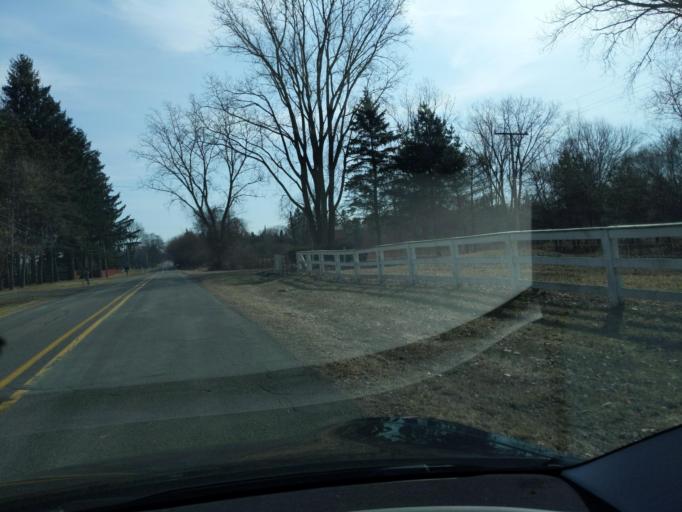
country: US
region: Michigan
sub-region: Ingham County
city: Williamston
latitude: 42.6588
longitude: -84.3045
